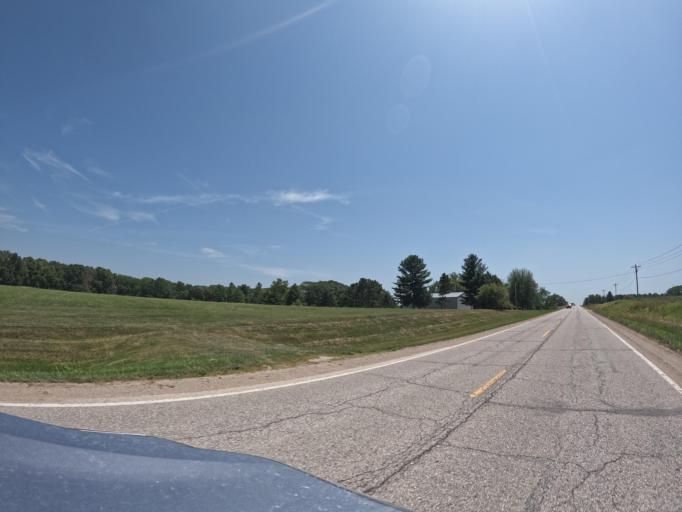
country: US
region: Iowa
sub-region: Henry County
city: Mount Pleasant
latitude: 40.9647
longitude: -91.6124
